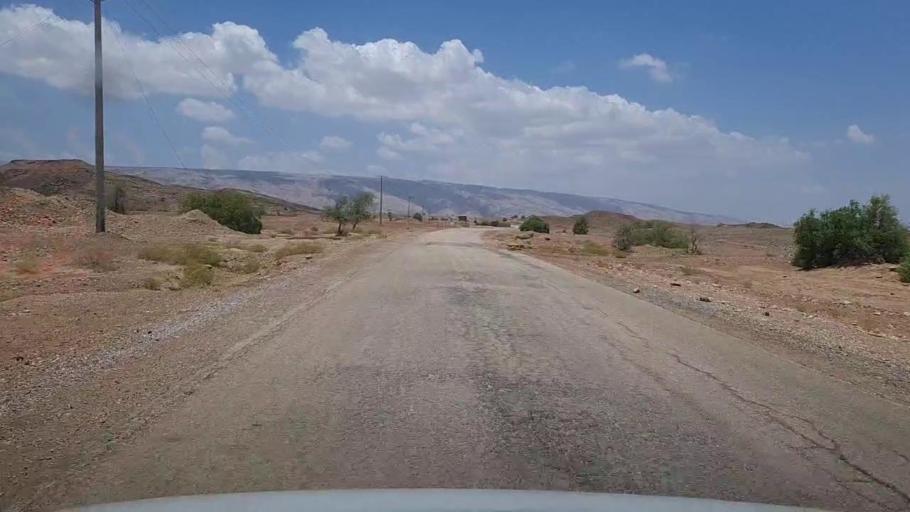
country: PK
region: Sindh
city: Bhan
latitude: 26.3170
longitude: 67.5633
